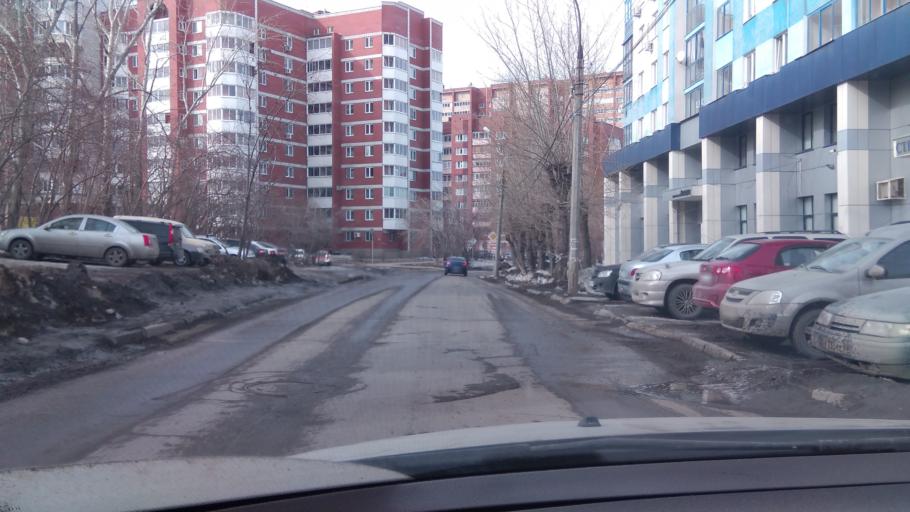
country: RU
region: Sverdlovsk
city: Sovkhoznyy
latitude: 56.7660
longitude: 60.6082
